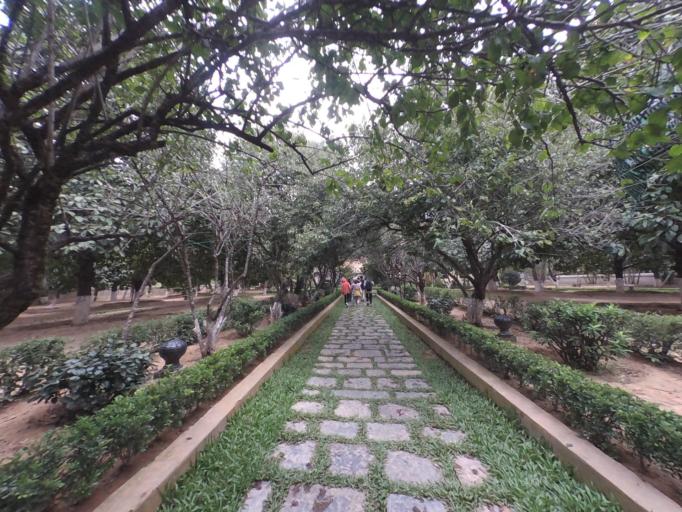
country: VN
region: Thua Thien-Hue
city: Hue
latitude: 16.4549
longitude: 107.5539
